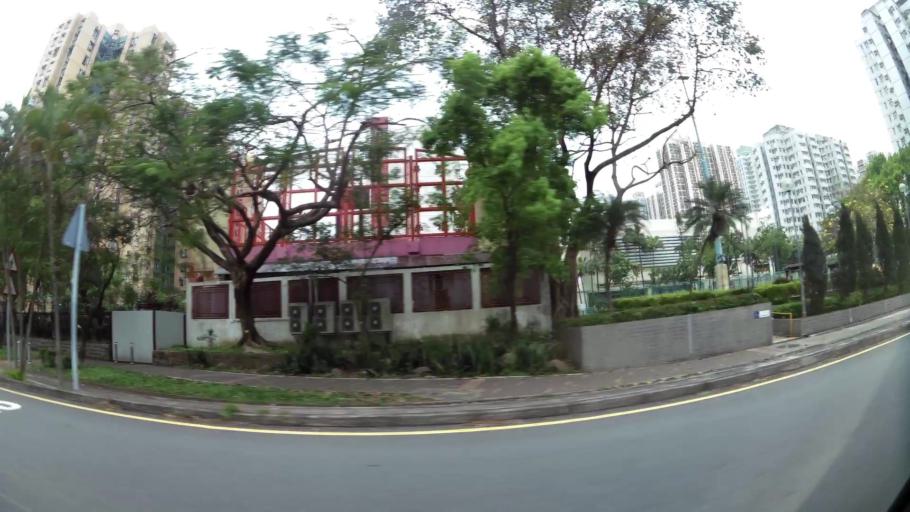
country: HK
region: Tai Po
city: Tai Po
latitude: 22.4544
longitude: 114.1661
